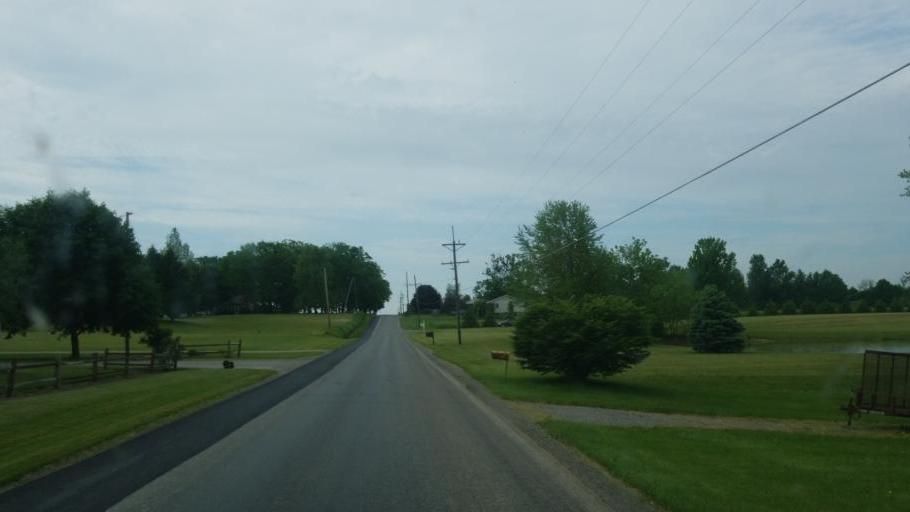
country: US
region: Ohio
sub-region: Wayne County
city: Dalton
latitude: 40.7799
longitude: -81.7551
